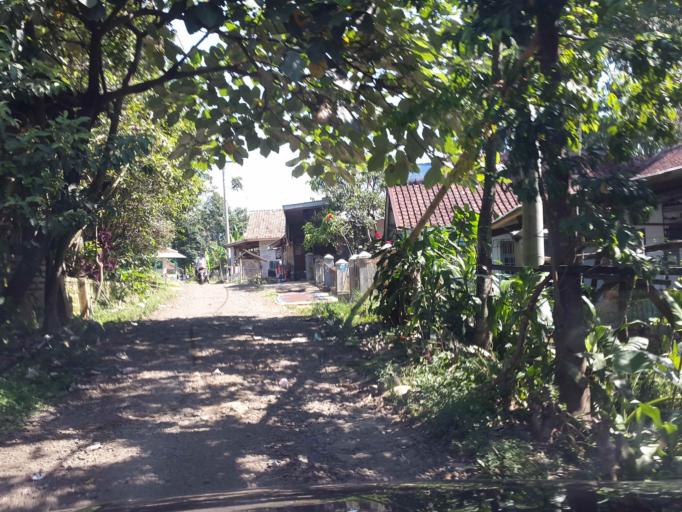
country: ID
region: West Java
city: Ciranjang-hilir
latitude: -6.7555
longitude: 107.1377
